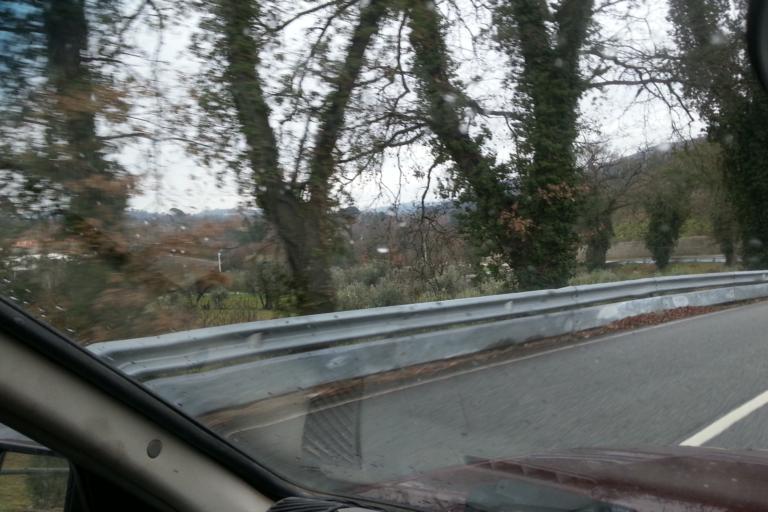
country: PT
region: Viseu
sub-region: Viseu
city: Rio de Loba
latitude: 40.6361
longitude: -7.8320
